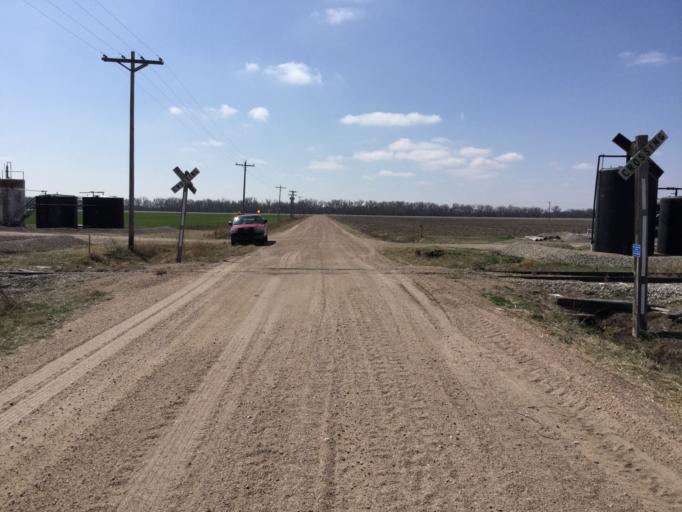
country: US
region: Kansas
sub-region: Barton County
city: Ellinwood
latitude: 38.3522
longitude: -98.5539
